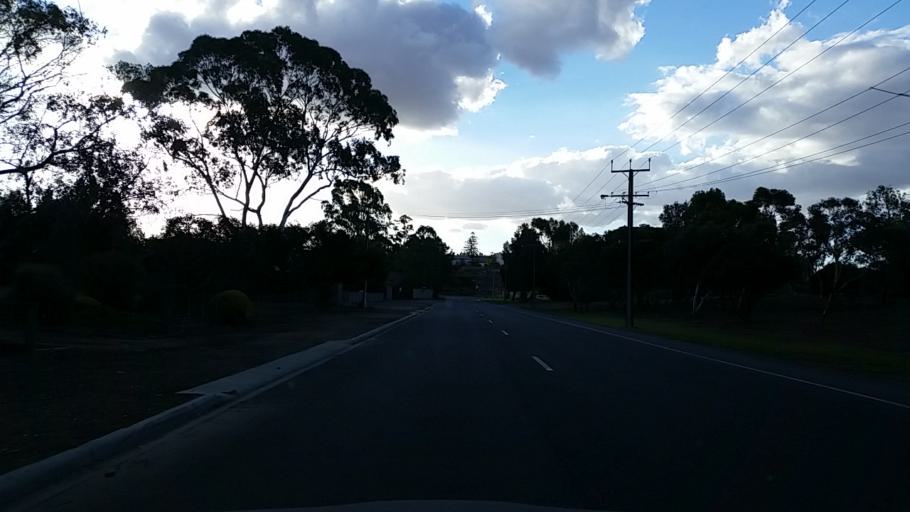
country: AU
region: South Australia
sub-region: Murray Bridge
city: Murray Bridge
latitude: -35.1234
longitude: 139.2810
